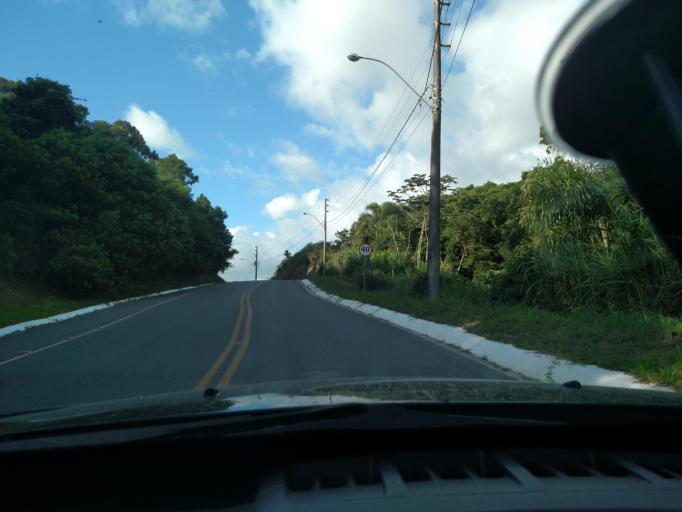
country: BR
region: Santa Catarina
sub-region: Porto Belo
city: Porto Belo
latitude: -27.1608
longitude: -48.4936
